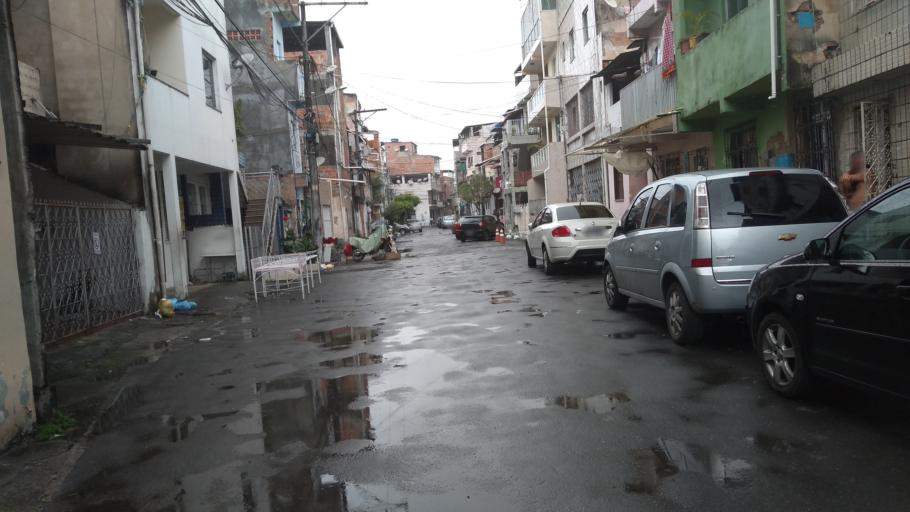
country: BR
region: Bahia
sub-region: Salvador
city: Salvador
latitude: -12.9187
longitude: -38.4987
